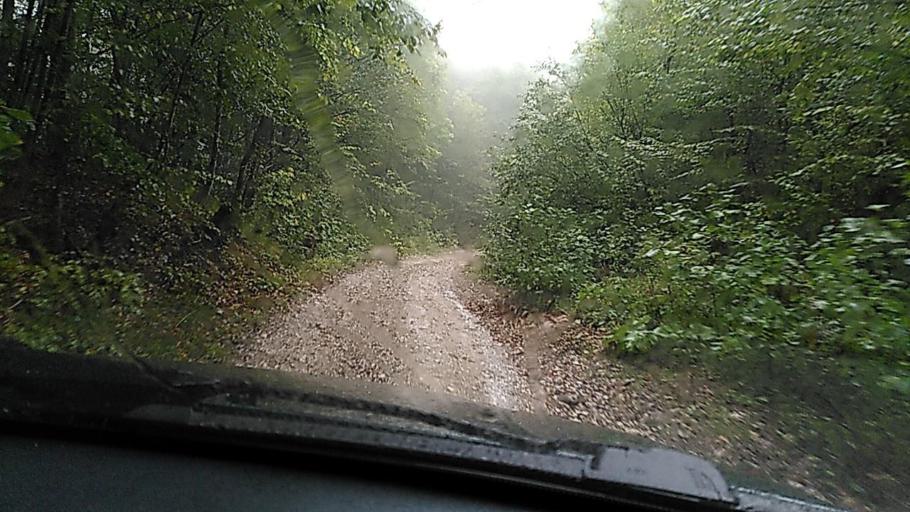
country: RU
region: Kabardino-Balkariya
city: Belaya Rechka
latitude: 43.3744
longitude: 43.4289
